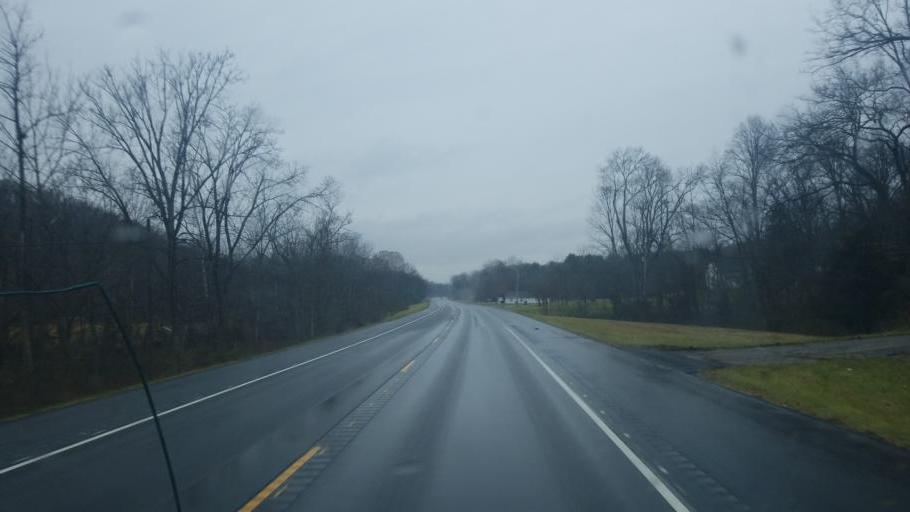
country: US
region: Indiana
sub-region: Brown County
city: Nashville
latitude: 39.1904
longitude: -86.1811
